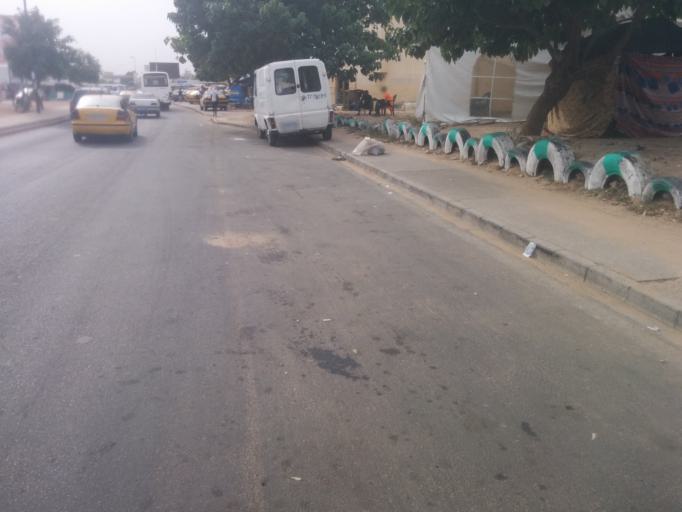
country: SN
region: Dakar
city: Grand Dakar
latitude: 14.7298
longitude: -17.4582
